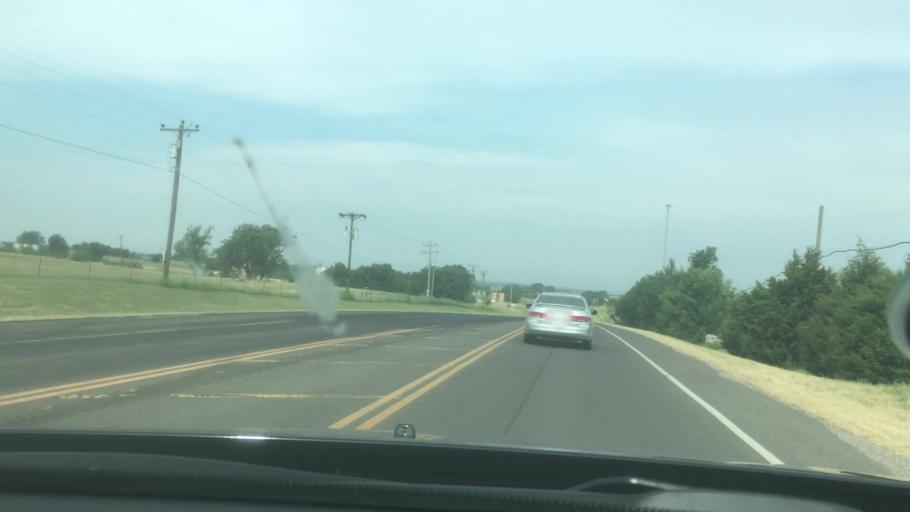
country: US
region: Oklahoma
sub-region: Garvin County
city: Maysville
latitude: 34.8192
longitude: -97.4426
